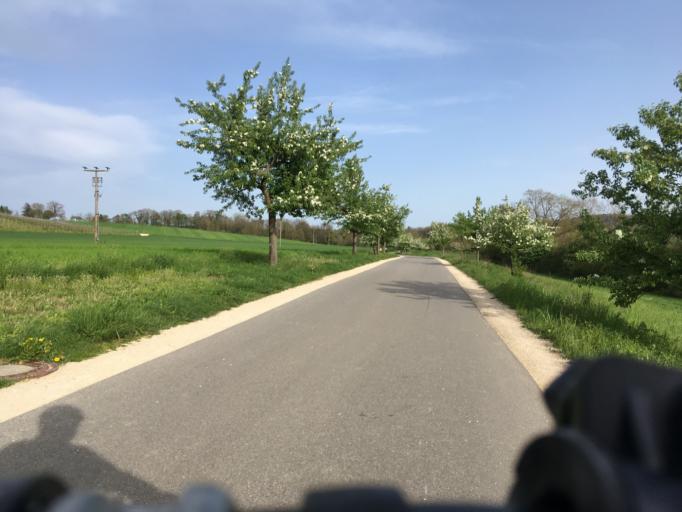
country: DE
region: Baden-Wuerttemberg
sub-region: Freiburg Region
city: Gailingen
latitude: 47.6882
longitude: 8.7647
